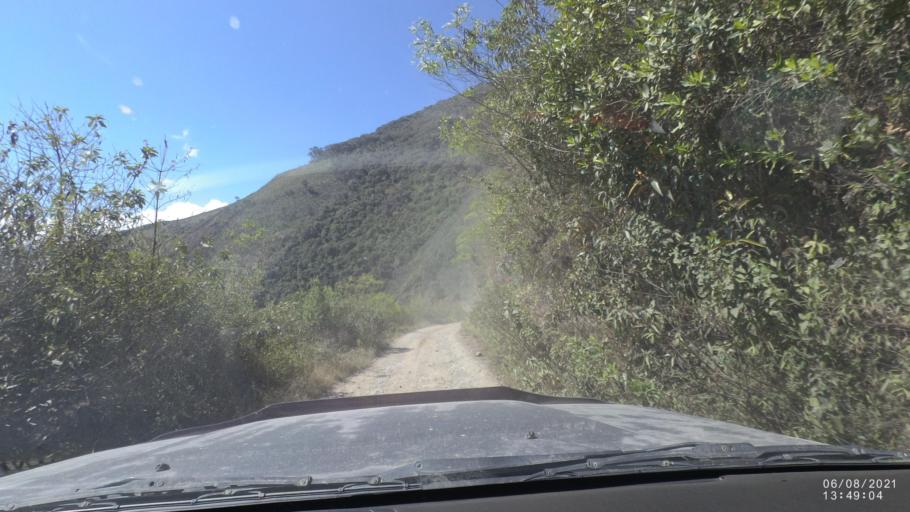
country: BO
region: La Paz
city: Quime
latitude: -16.6619
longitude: -66.7235
